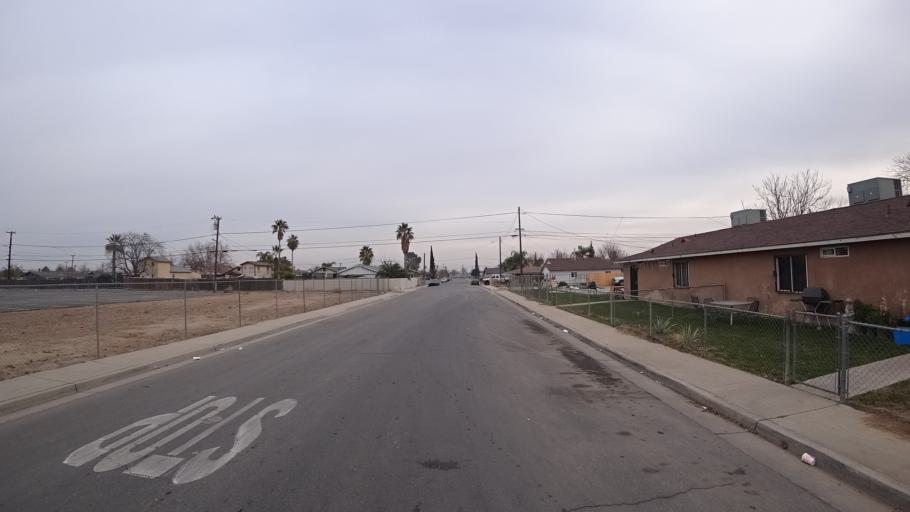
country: US
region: California
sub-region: Kern County
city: Bakersfield
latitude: 35.3636
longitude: -118.9839
